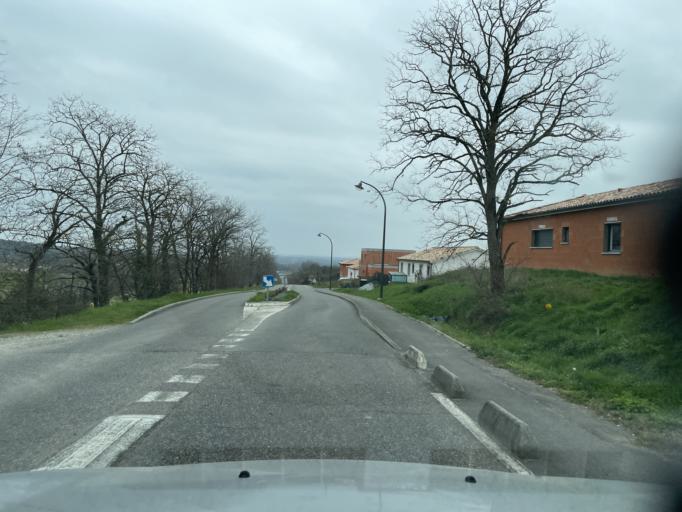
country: FR
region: Midi-Pyrenees
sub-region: Departement du Gers
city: Pujaudran
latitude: 43.5891
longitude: 1.1593
